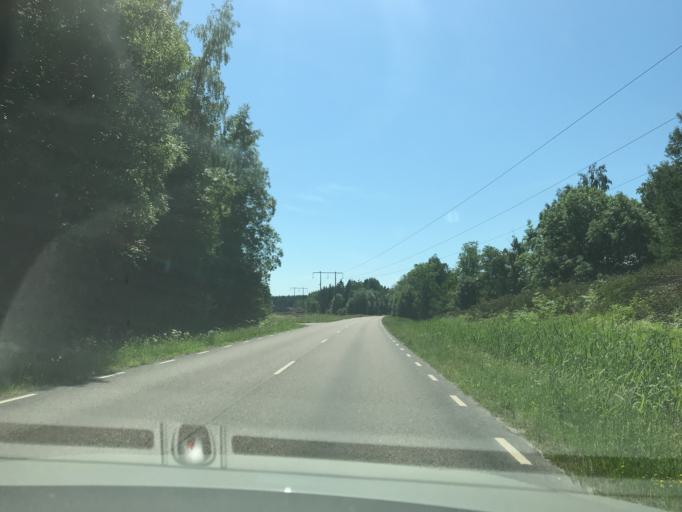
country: SE
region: Vaestra Goetaland
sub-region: Gotene Kommun
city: Kallby
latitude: 58.6013
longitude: 13.3940
